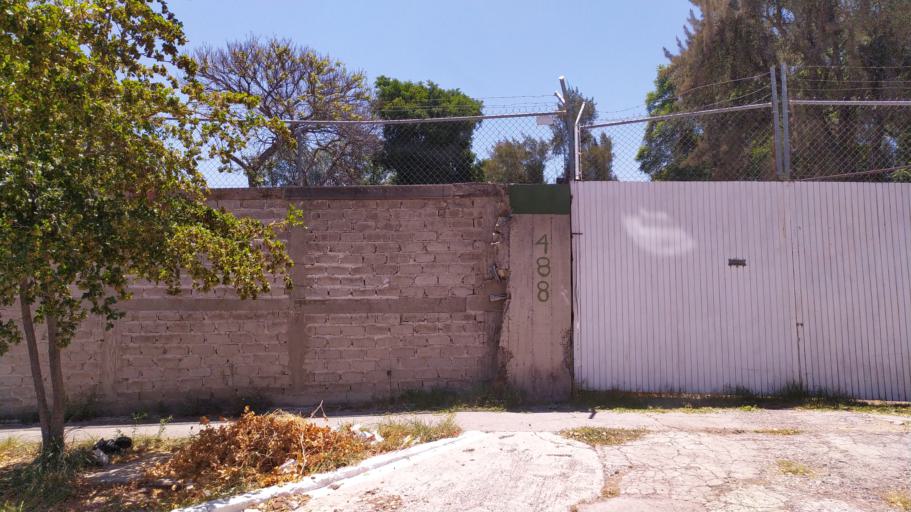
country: MX
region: Jalisco
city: Guadalajara
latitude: 20.6824
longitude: -103.4085
